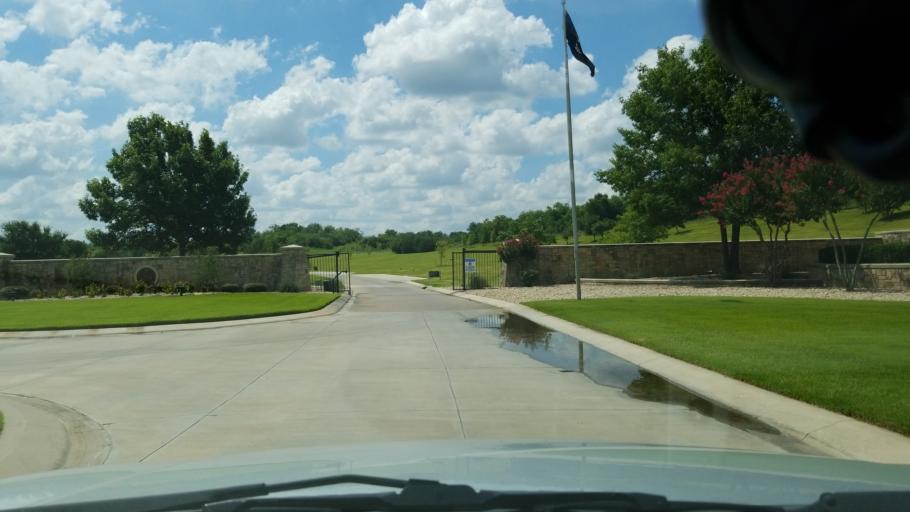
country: US
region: Texas
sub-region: Dallas County
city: Grand Prairie
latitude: 32.7177
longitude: -96.9470
